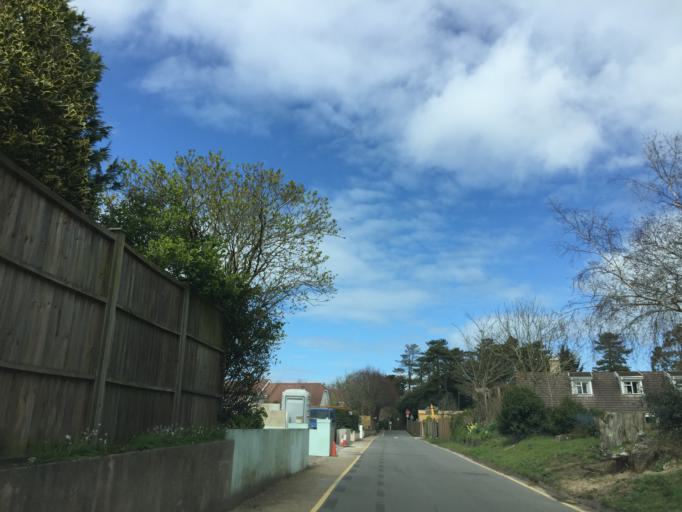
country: JE
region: St Helier
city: Saint Helier
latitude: 49.1909
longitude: -2.1952
